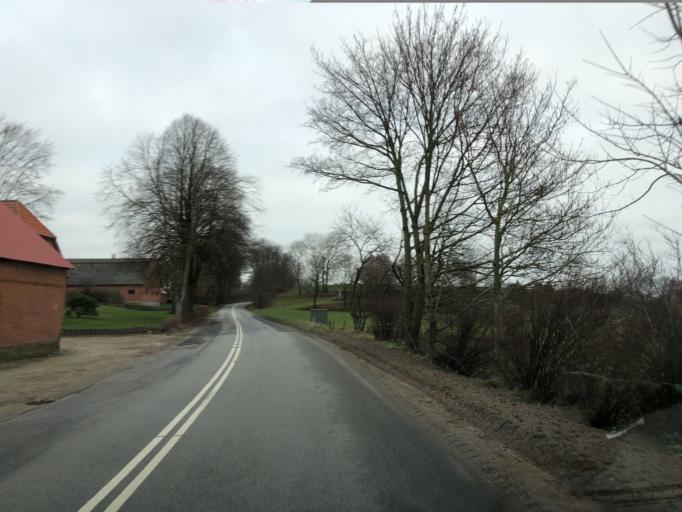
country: DK
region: Central Jutland
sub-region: Viborg Kommune
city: Stoholm
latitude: 56.4720
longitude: 9.1478
